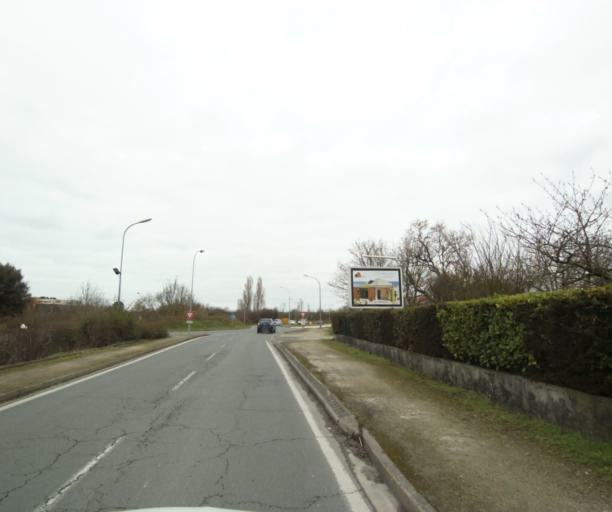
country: FR
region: Poitou-Charentes
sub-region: Departement de la Charente-Maritime
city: Lagord
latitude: 46.1778
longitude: -1.1519
